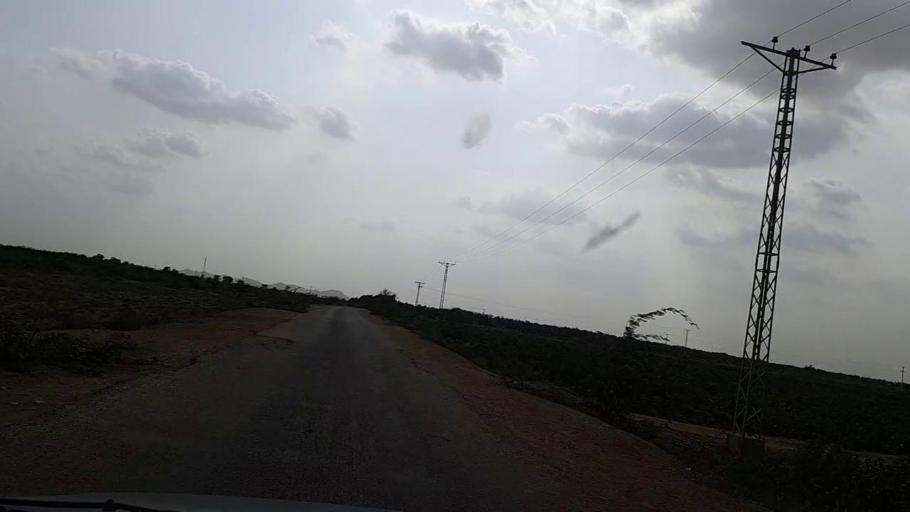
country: PK
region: Sindh
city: Kotri
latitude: 25.2570
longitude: 68.2470
